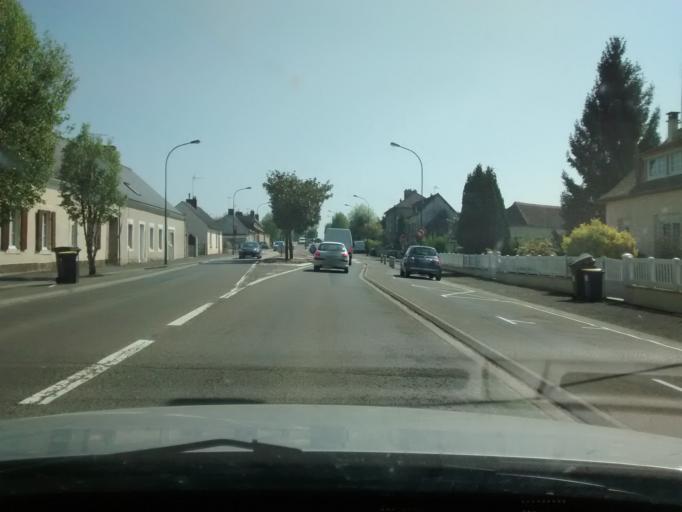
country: FR
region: Pays de la Loire
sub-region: Departement de la Sarthe
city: Trange
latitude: 48.0254
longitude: 0.0750
